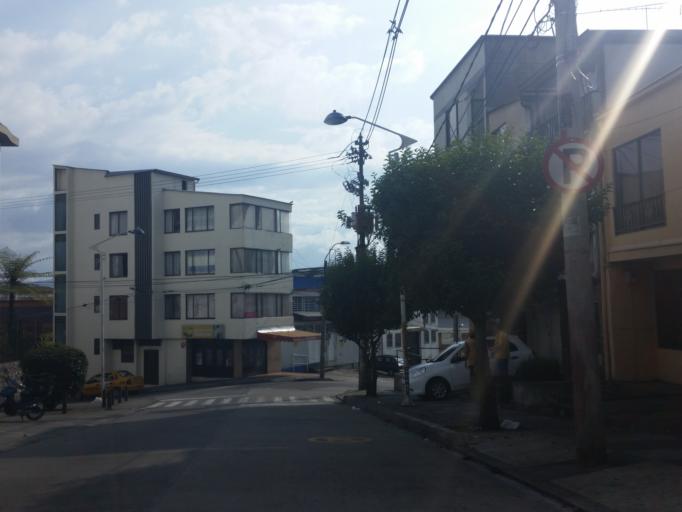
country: CO
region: Caldas
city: Manizales
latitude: 5.0626
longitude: -75.5013
